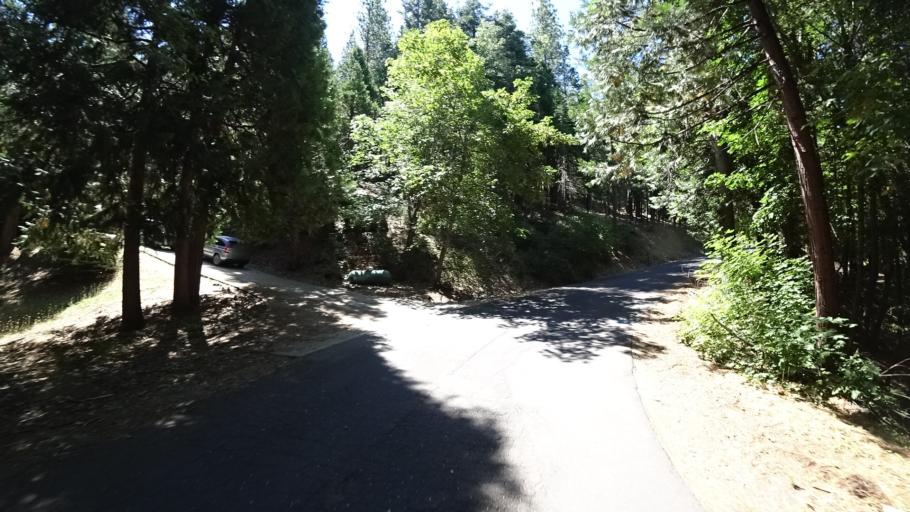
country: US
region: California
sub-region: Calaveras County
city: Arnold
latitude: 38.2375
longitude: -120.3321
